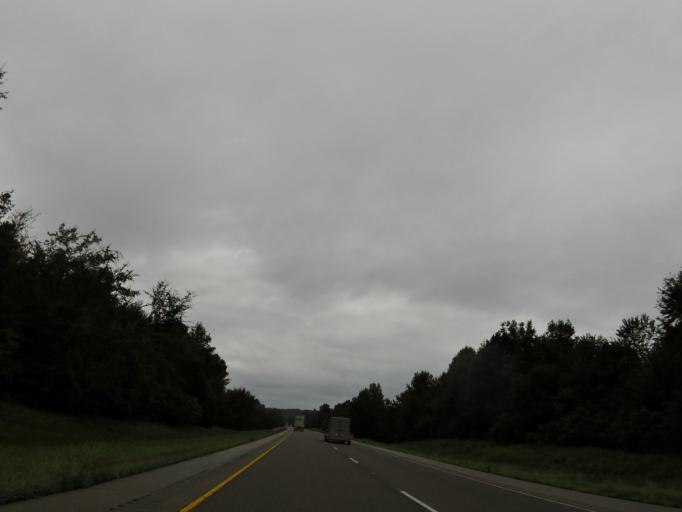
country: US
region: Illinois
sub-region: Johnson County
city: Vienna
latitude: 37.3684
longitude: -88.8038
